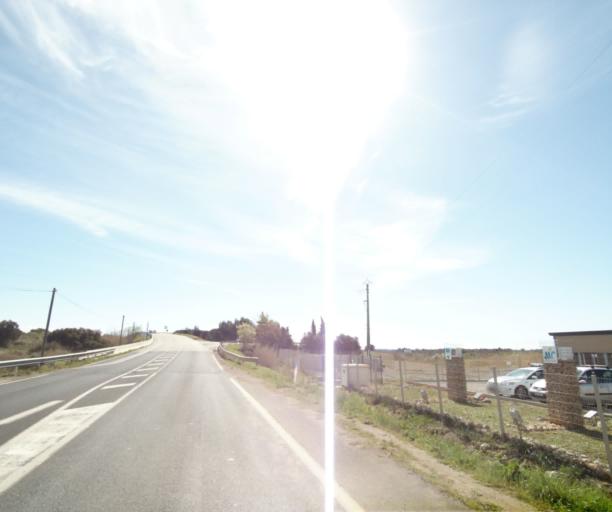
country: FR
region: Languedoc-Roussillon
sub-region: Departement de l'Herault
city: Saint-Jean-de-Vedas
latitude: 43.5456
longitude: 3.8203
